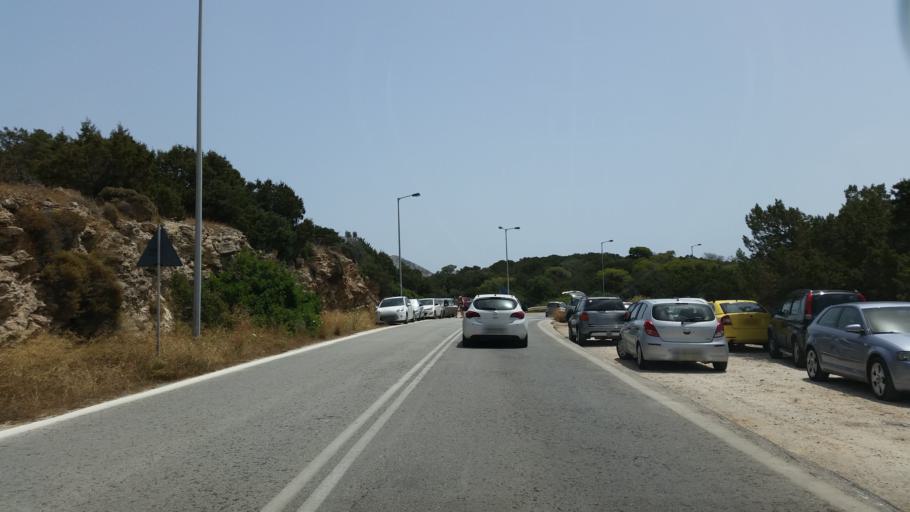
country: GR
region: Attica
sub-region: Nomarchia Anatolikis Attikis
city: Palaia Fokaia
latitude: 37.6899
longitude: 23.9389
